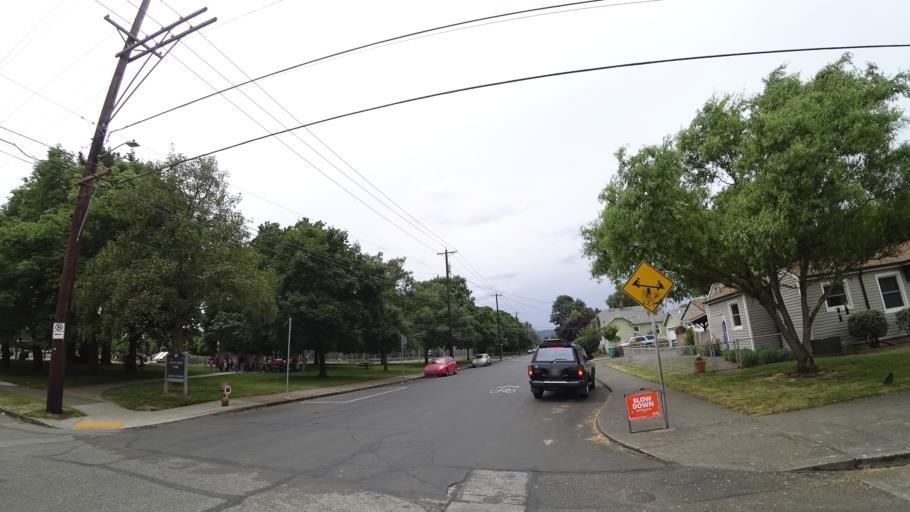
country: US
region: Oregon
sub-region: Multnomah County
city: Portland
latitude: 45.5736
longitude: -122.6925
